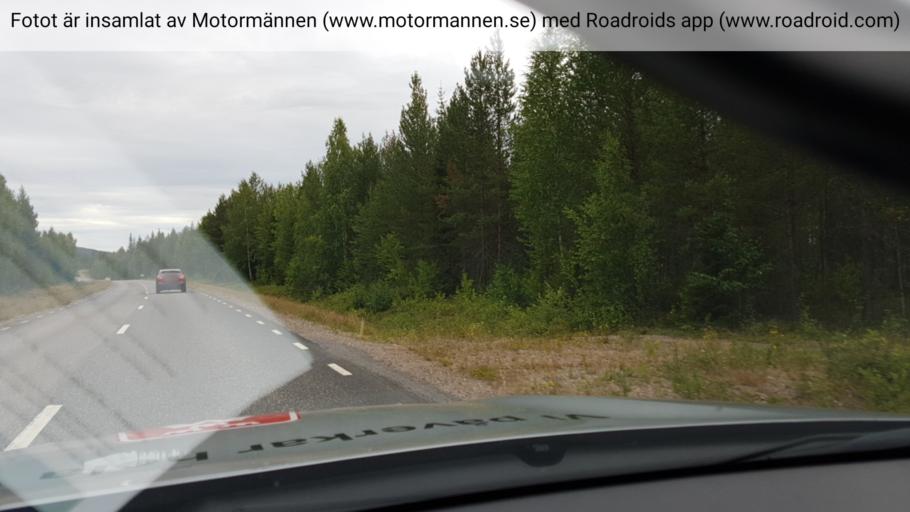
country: SE
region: Norrbotten
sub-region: Overkalix Kommun
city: OEverkalix
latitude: 66.5278
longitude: 22.7578
